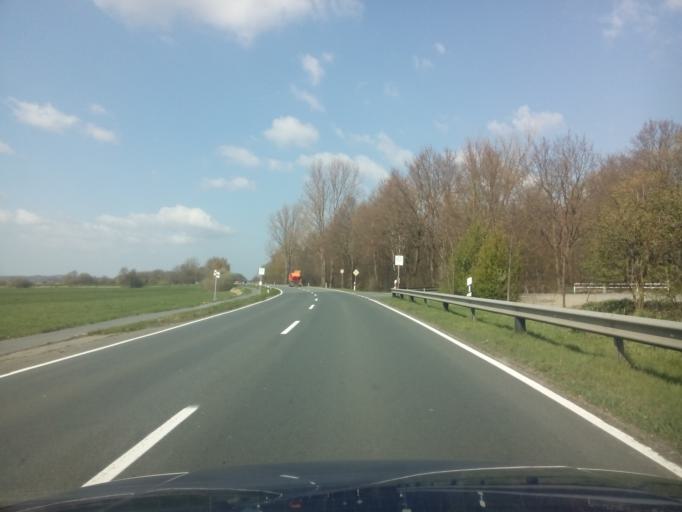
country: DE
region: Lower Saxony
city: Osterholz-Scharmbeck
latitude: 53.1903
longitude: 8.8211
